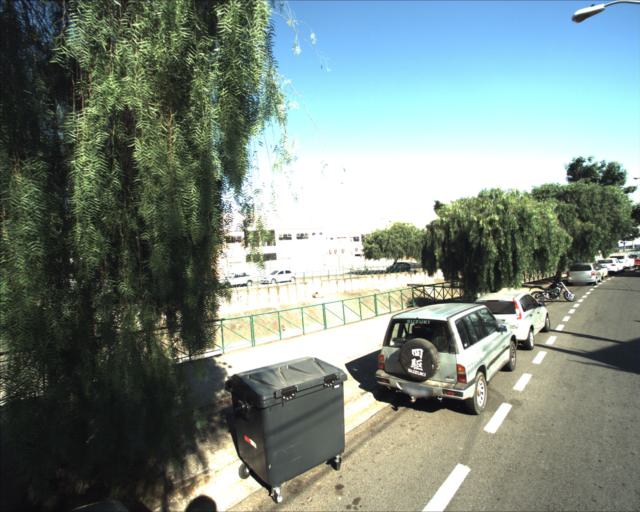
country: BR
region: Sao Paulo
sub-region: Sorocaba
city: Sorocaba
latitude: -23.5120
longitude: -47.4293
